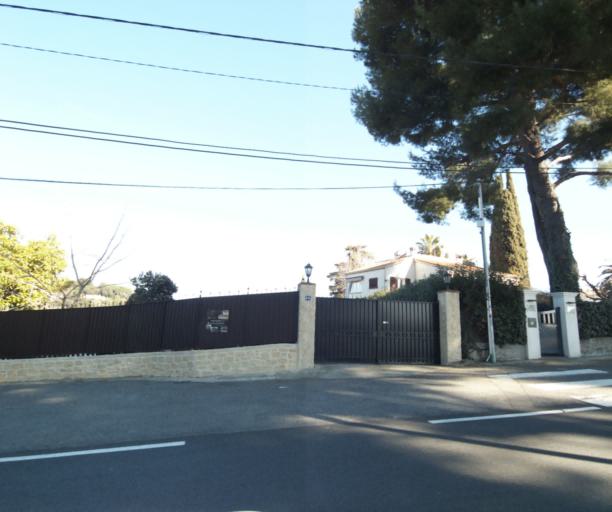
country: FR
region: Provence-Alpes-Cote d'Azur
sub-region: Departement des Alpes-Maritimes
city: Biot
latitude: 43.6045
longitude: 7.0922
